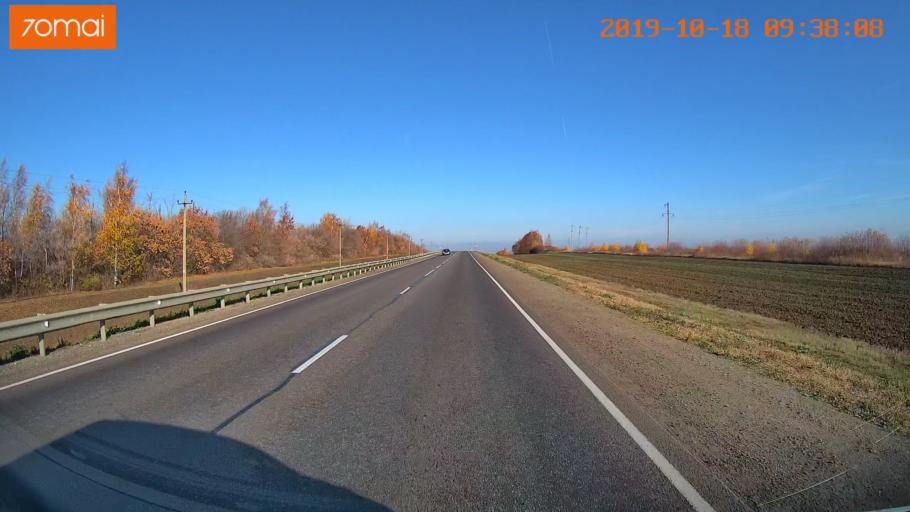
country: RU
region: Tula
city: Yefremov
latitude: 53.2333
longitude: 38.1383
